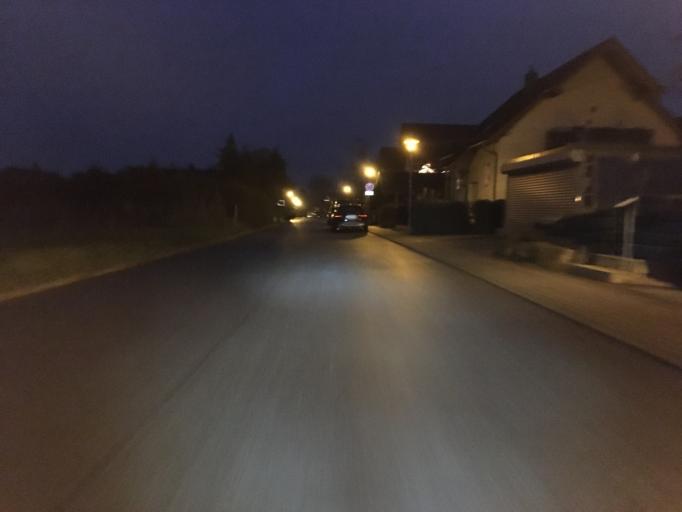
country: DE
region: Baden-Wuerttemberg
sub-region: Karlsruhe Region
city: Ettlingen
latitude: 48.9144
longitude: 8.4975
